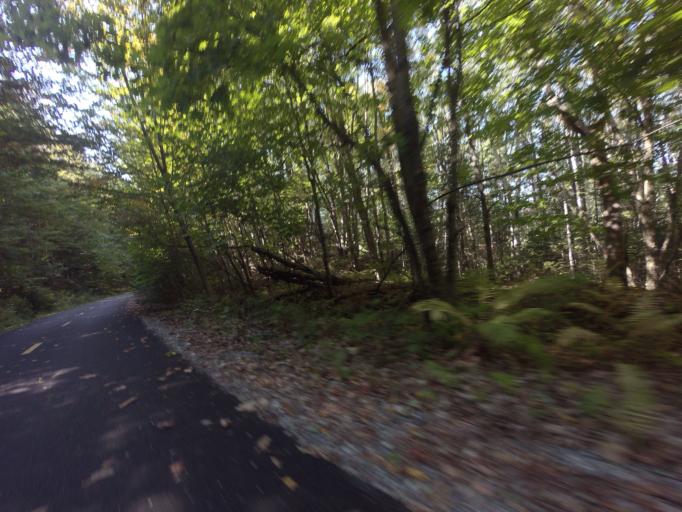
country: CA
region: Quebec
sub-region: Laurentides
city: Mont-Tremblant
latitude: 46.1330
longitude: -74.4841
